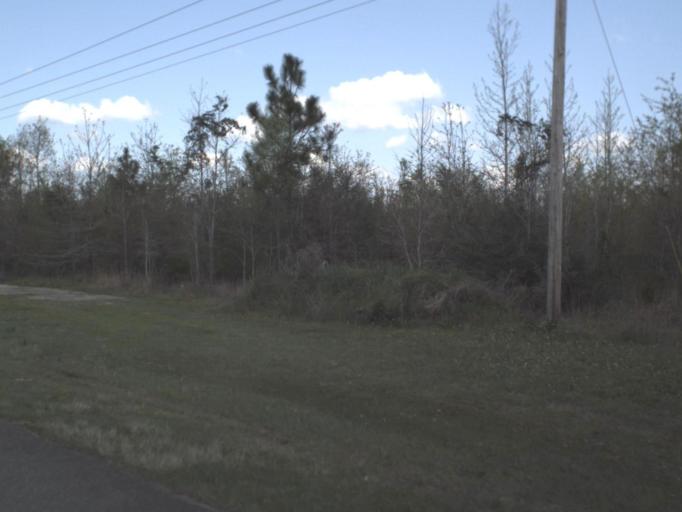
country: US
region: Alabama
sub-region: Escambia County
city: East Brewton
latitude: 30.9484
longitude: -87.0754
